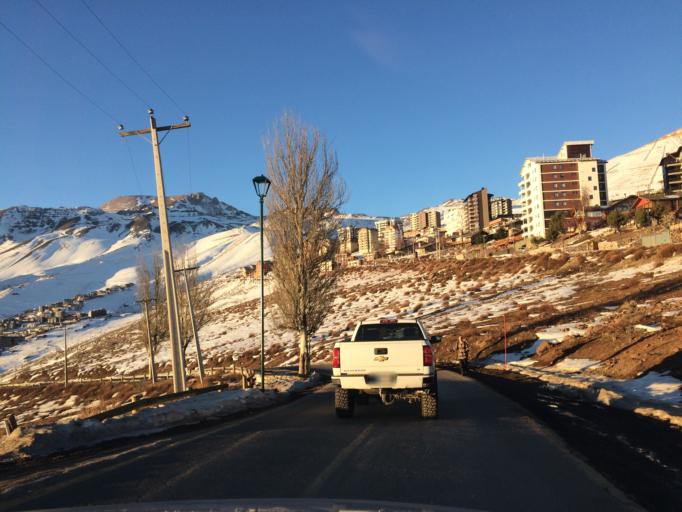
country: CL
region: Santiago Metropolitan
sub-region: Provincia de Santiago
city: Villa Presidente Frei, Nunoa, Santiago, Chile
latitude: -33.3502
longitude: -70.2968
